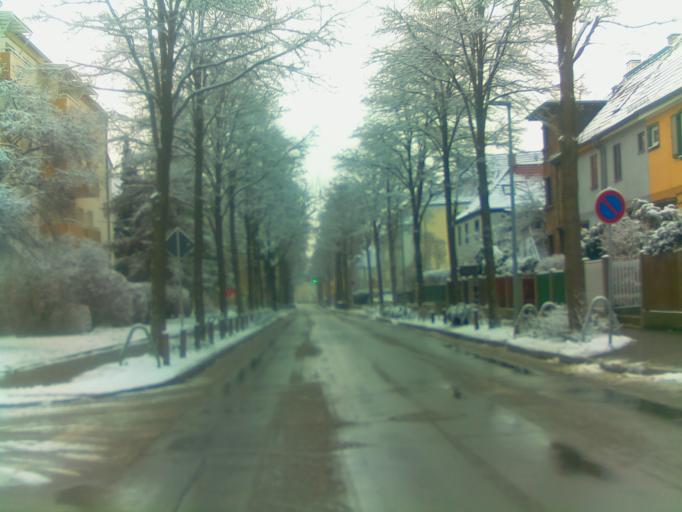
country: DE
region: Thuringia
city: Arnstadt
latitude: 50.8382
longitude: 10.9326
